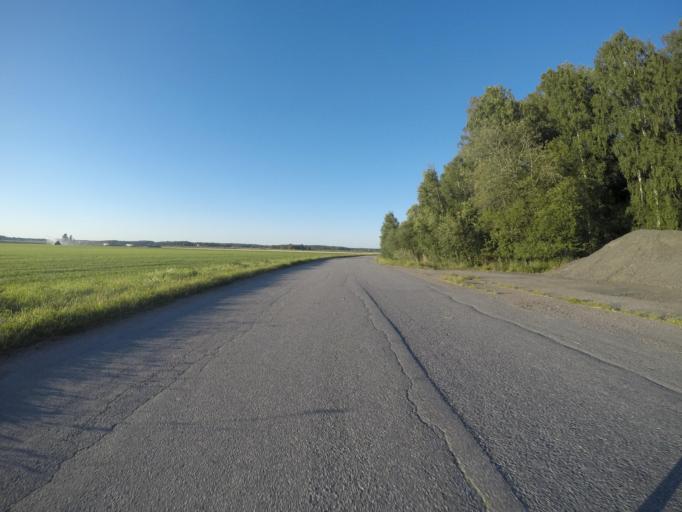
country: SE
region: Vaestmanland
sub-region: Vasteras
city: Vasteras
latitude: 59.5764
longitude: 16.6546
